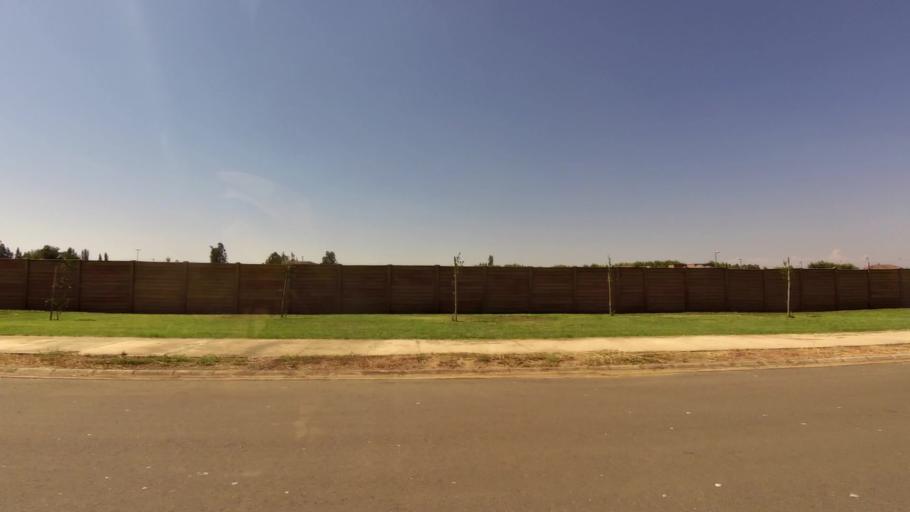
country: CL
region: Maule
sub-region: Provincia de Talca
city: Talca
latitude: -35.4311
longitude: -71.6001
